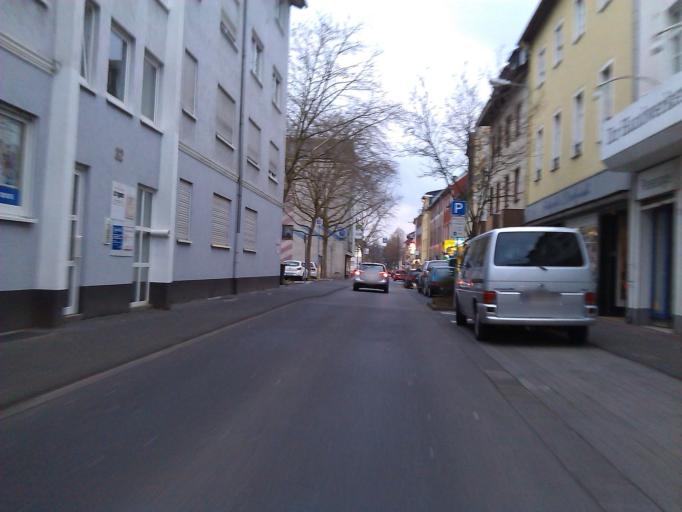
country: DE
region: Rheinland-Pfalz
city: Lahnstein
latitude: 50.3015
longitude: 7.6063
